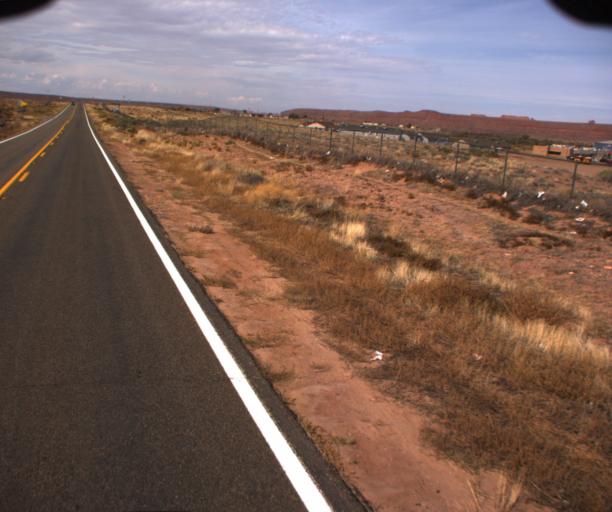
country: US
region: Arizona
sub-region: Apache County
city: Many Farms
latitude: 36.5103
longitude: -109.4746
